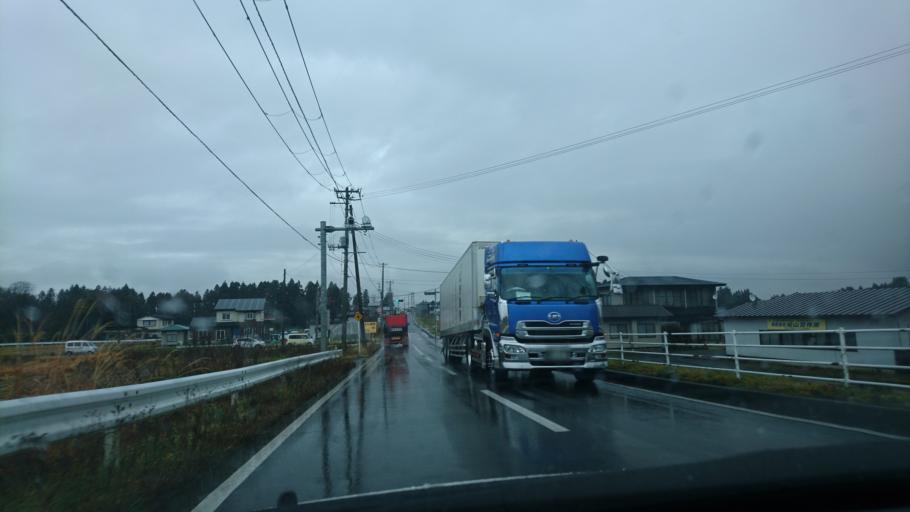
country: JP
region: Iwate
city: Kitakami
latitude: 39.2920
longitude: 141.0550
